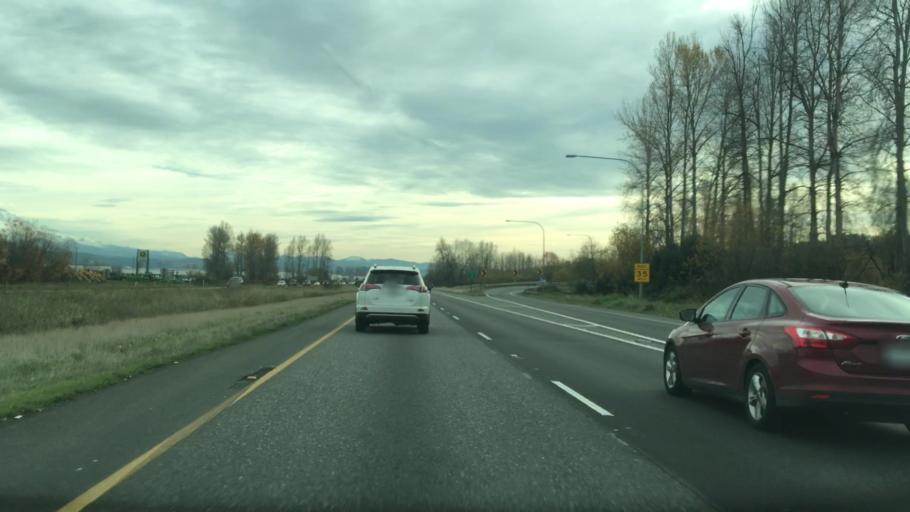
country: US
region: Washington
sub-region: King County
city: Pacific
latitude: 47.2346
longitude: -122.2516
